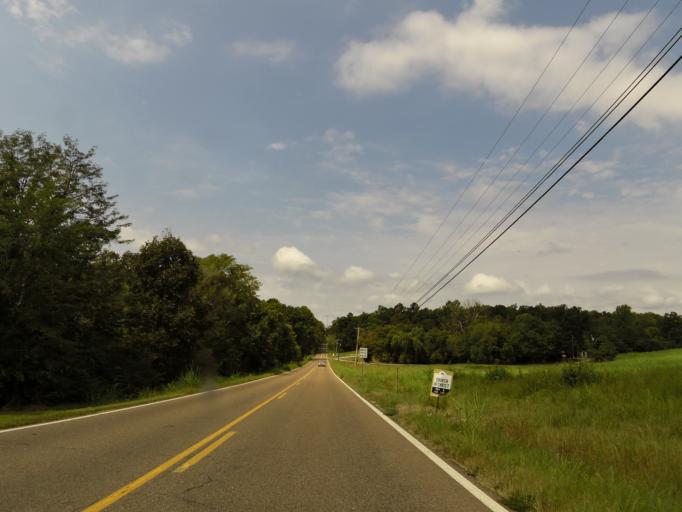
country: US
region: Tennessee
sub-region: Decatur County
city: Decaturville
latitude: 35.5821
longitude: -88.1084
